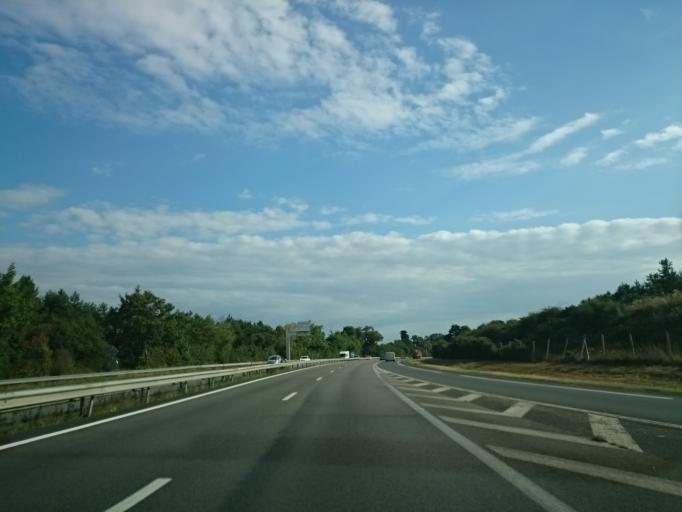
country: FR
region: Pays de la Loire
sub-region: Departement de la Loire-Atlantique
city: Heric
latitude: 47.4138
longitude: -1.6417
